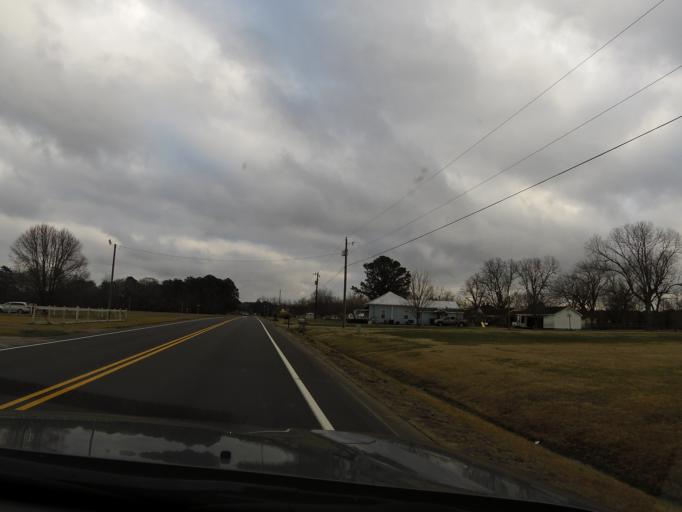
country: US
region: North Carolina
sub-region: Nash County
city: Rocky Mount
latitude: 35.8670
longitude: -77.7299
